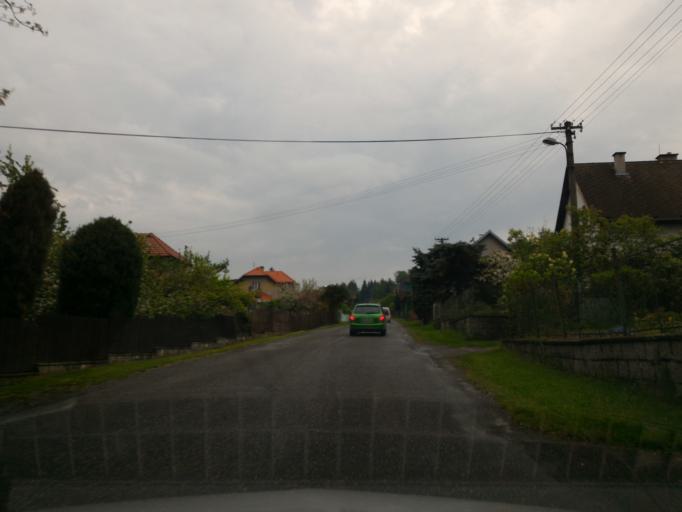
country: CZ
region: Vysocina
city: Ledec nad Sazavou
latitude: 49.6473
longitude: 15.2943
